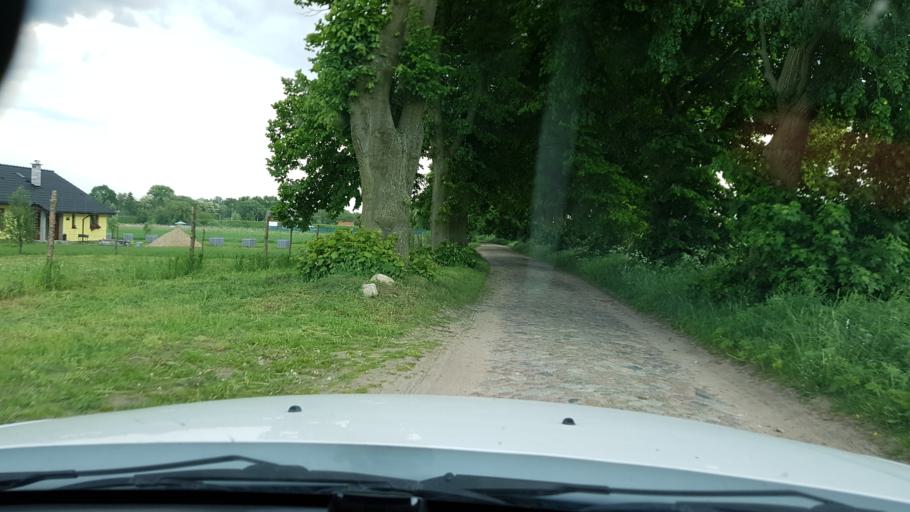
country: PL
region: West Pomeranian Voivodeship
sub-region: Powiat stargardzki
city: Stara Dabrowa
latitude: 53.3751
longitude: 15.1733
